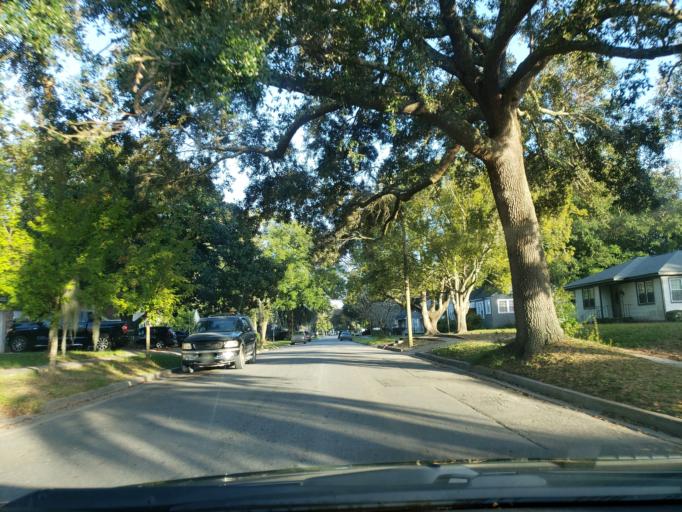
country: US
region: Georgia
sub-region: Chatham County
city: Thunderbolt
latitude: 32.0519
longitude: -81.0761
